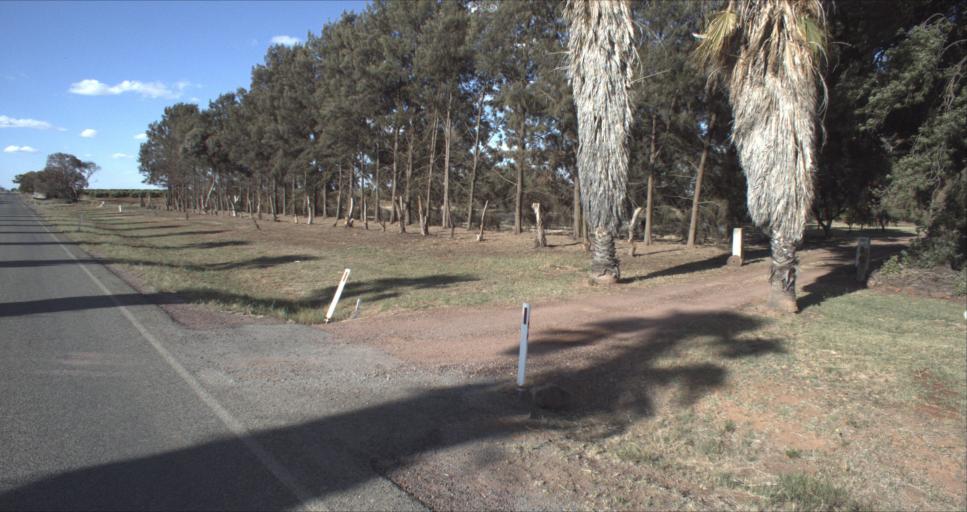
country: AU
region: New South Wales
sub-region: Leeton
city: Leeton
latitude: -34.5244
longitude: 146.2827
